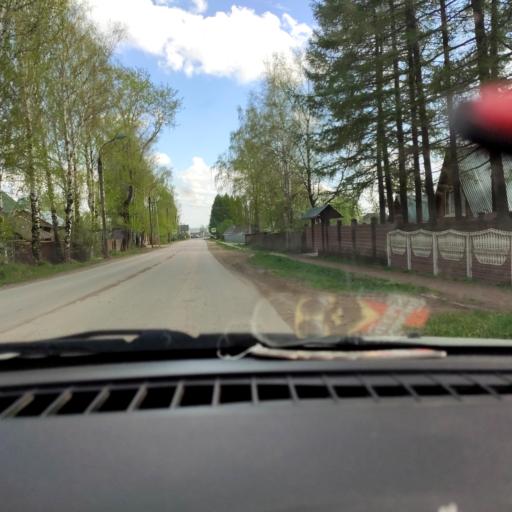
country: RU
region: Perm
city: Kudymkar
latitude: 59.0171
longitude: 54.6508
